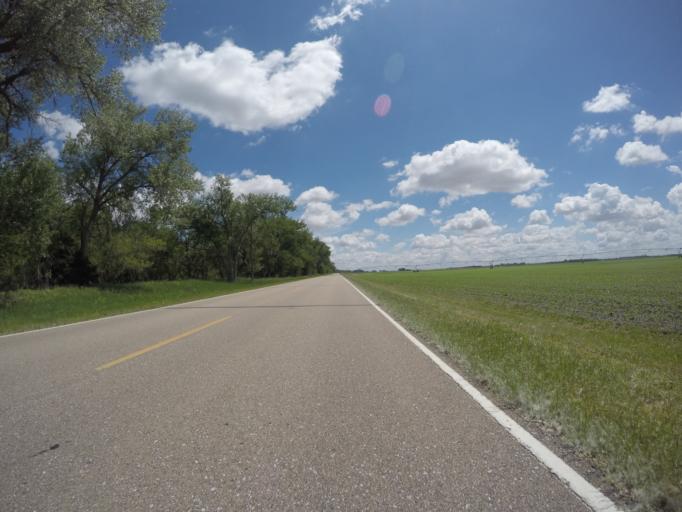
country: US
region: Nebraska
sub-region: Buffalo County
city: Kearney
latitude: 40.6546
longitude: -99.1157
